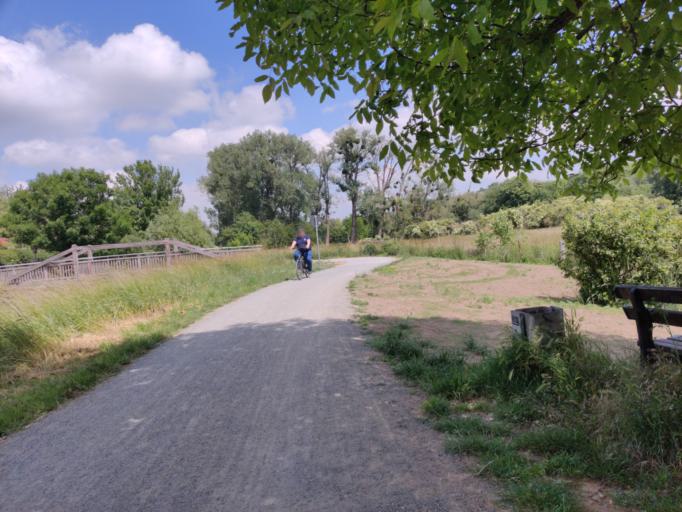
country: DE
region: Lower Saxony
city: Hildesheim
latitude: 52.1668
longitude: 9.9232
